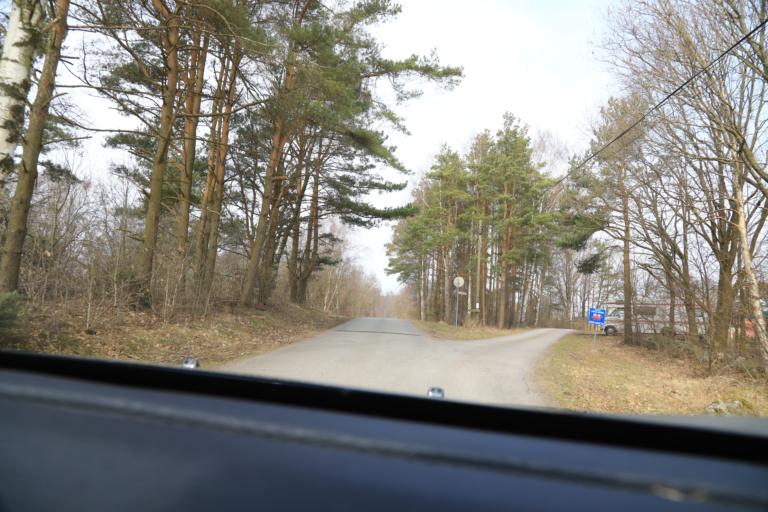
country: SE
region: Halland
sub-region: Kungsbacka Kommun
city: Frillesas
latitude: 57.2747
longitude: 12.1453
